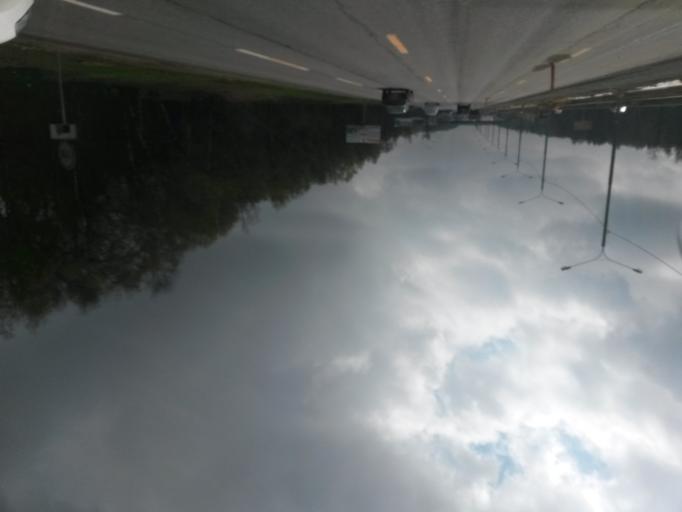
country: RU
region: Moskovskaya
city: Shcherbinka
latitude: 55.5063
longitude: 37.6091
